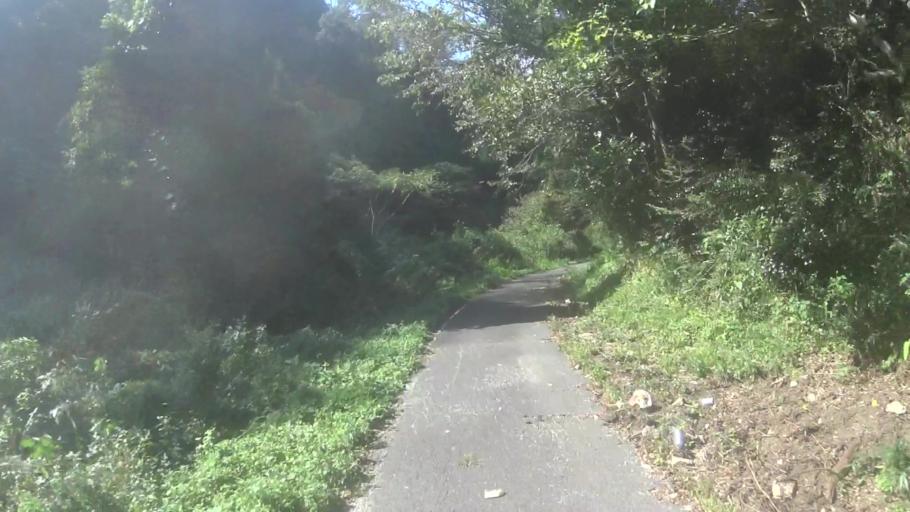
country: JP
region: Kyoto
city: Miyazu
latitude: 35.6994
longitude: 135.1259
